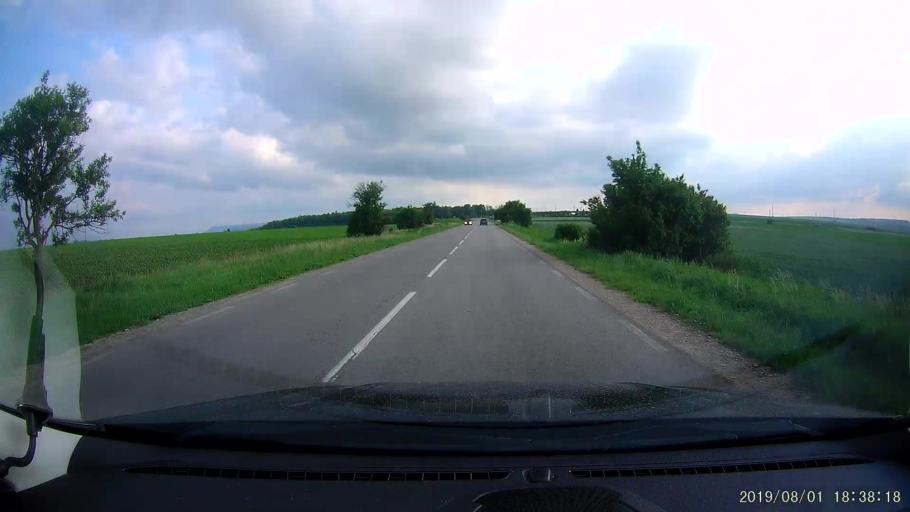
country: BG
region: Shumen
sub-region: Obshtina Khitrino
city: Gara Khitrino
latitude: 43.4043
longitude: 26.9185
